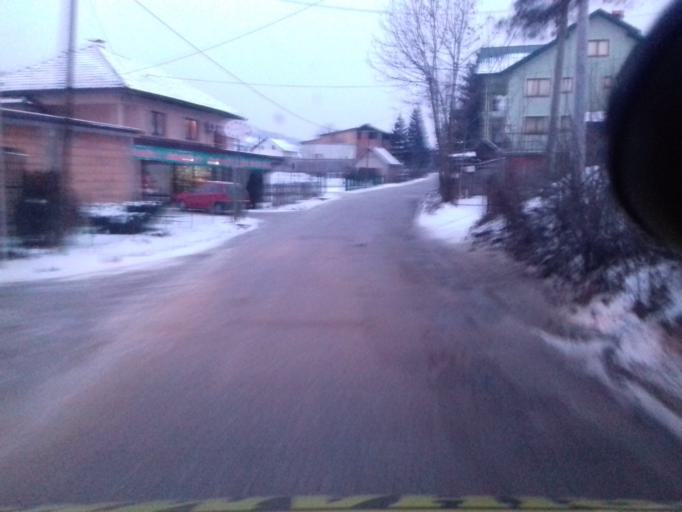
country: BA
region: Federation of Bosnia and Herzegovina
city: Vogosca
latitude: 43.8756
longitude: 18.3153
